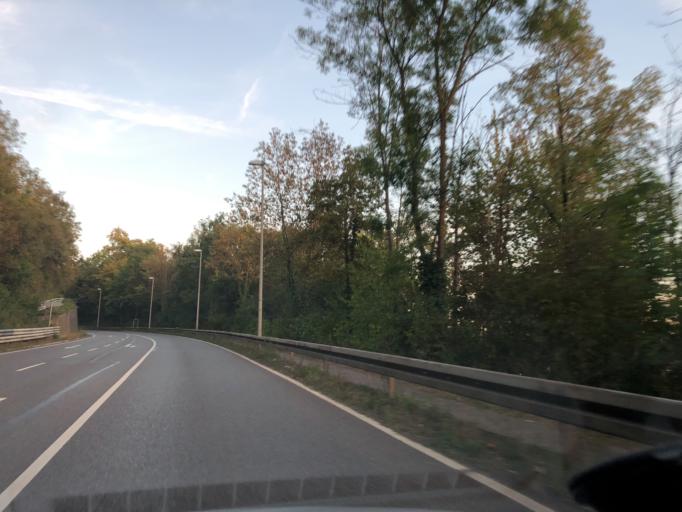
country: DE
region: Baden-Wuerttemberg
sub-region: Regierungsbezirk Stuttgart
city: Marbach am Neckar
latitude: 48.8903
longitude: 9.2721
